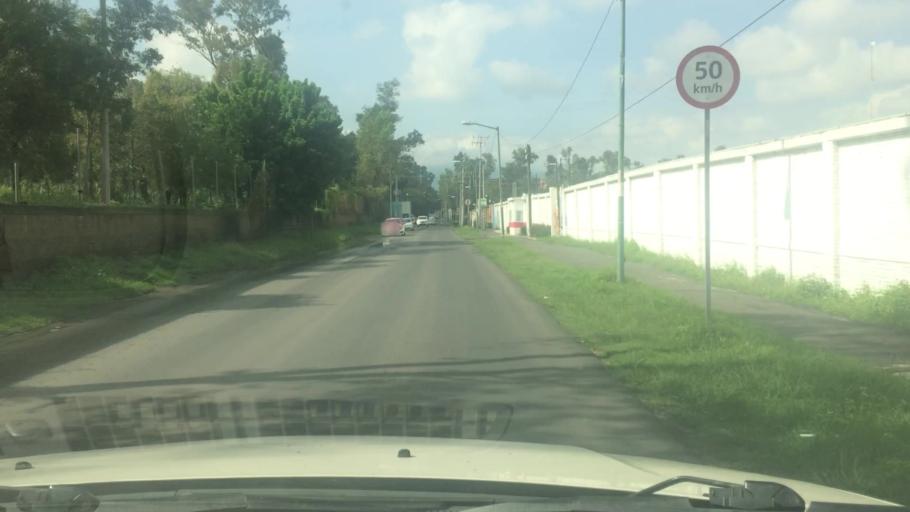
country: MX
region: Mexico City
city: Xochimilco
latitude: 19.3020
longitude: -99.1007
